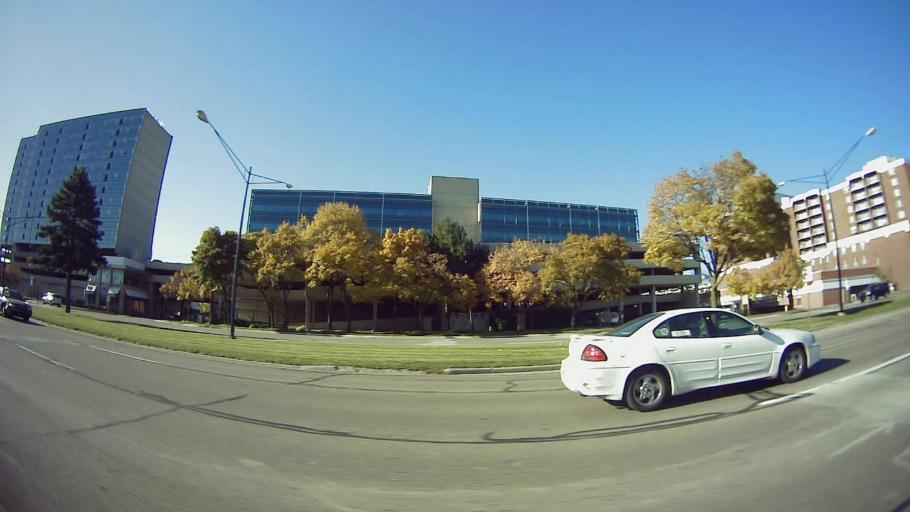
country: US
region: Michigan
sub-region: Oakland County
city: Birmingham
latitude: 42.5437
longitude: -83.2095
